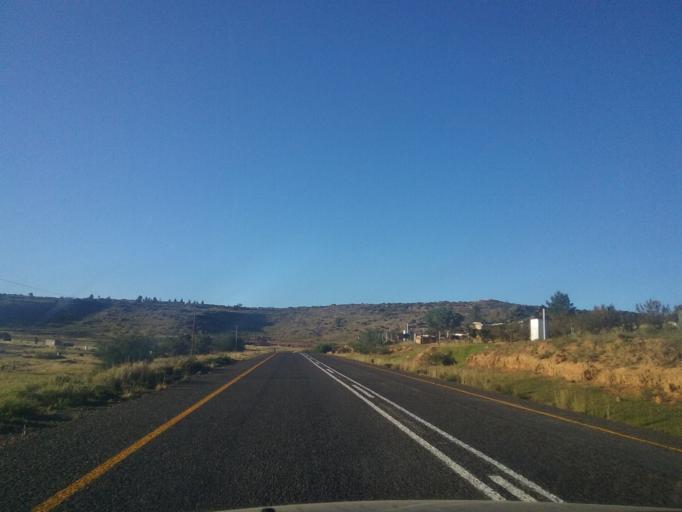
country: LS
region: Mohale's Hoek District
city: Mohale's Hoek
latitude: -30.2888
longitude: 27.4654
